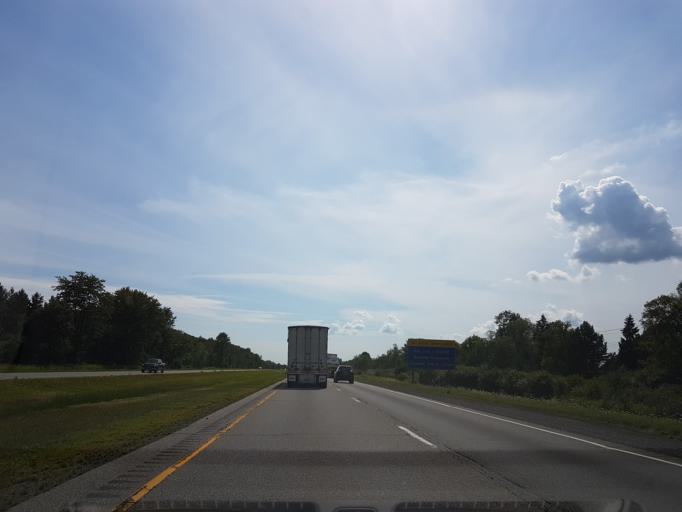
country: CA
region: Ontario
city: Prescott
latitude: 44.6864
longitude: -75.5864
